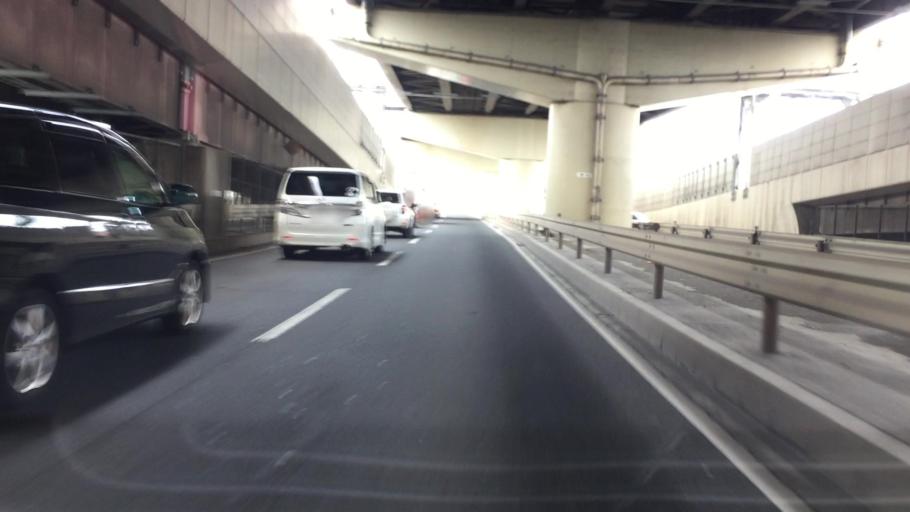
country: JP
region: Saitama
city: Yashio-shi
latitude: 35.8127
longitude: 139.8443
